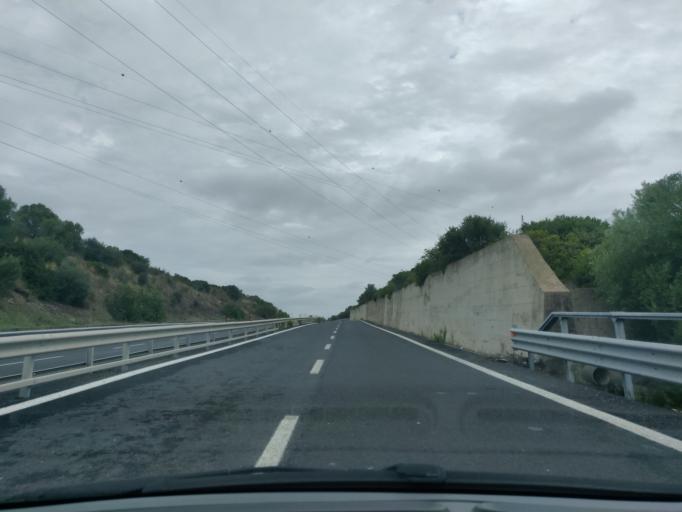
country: IT
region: Latium
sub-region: Citta metropolitana di Roma Capitale
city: Civitavecchia
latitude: 42.1126
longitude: 11.7925
